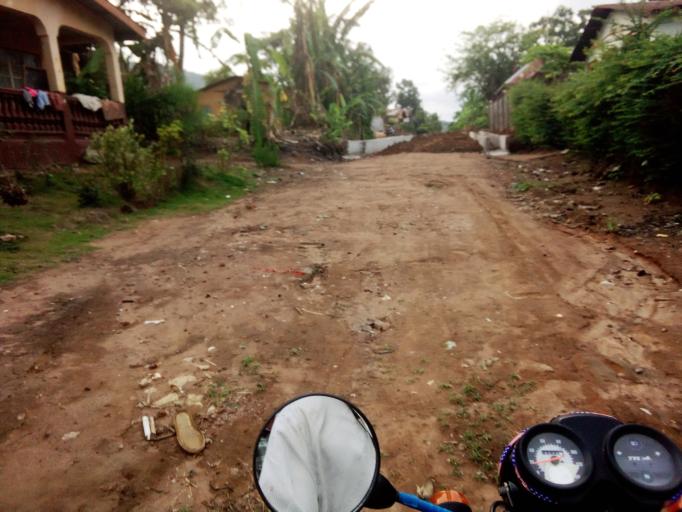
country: SL
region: Western Area
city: Waterloo
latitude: 8.3389
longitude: -13.0692
